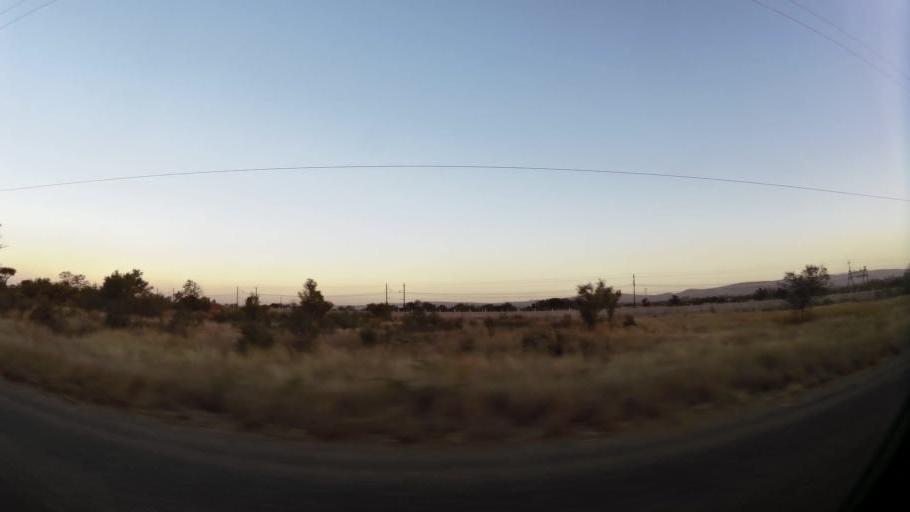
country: ZA
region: North-West
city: Ga-Rankuwa
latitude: -25.6218
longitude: 28.0282
